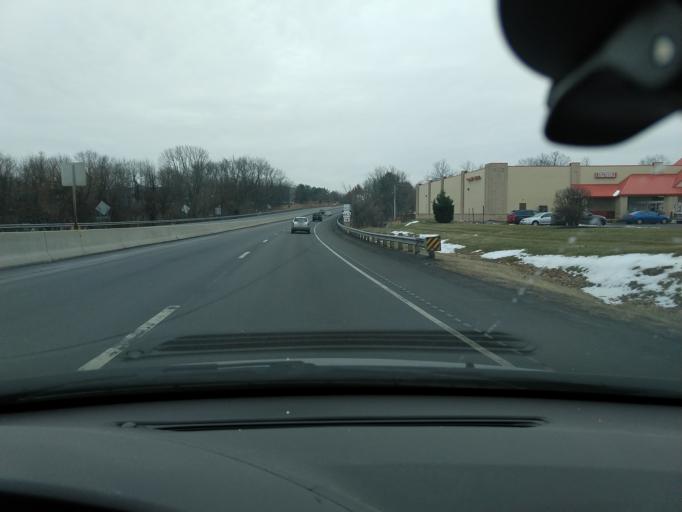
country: US
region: Pennsylvania
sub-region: Berks County
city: Boyertown
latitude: 40.3334
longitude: -75.6210
